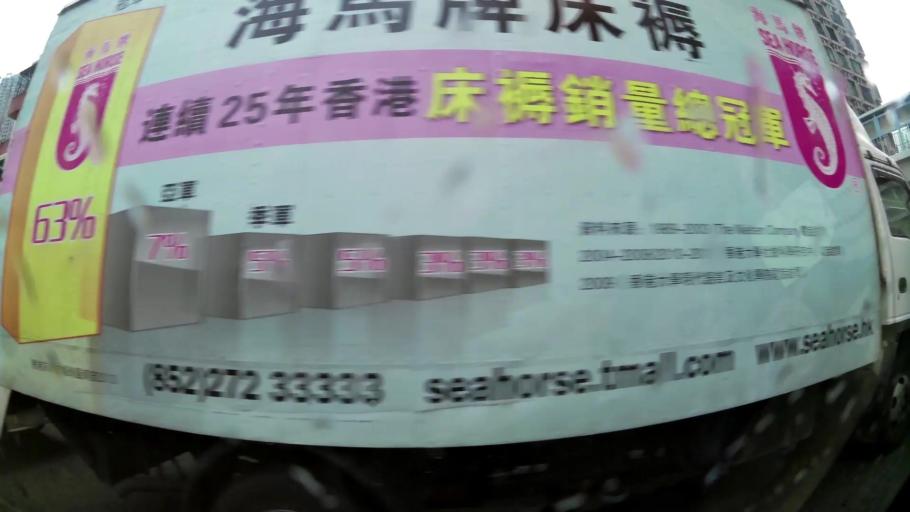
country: HK
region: Tsuen Wan
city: Tsuen Wan
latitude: 22.3668
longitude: 114.1175
